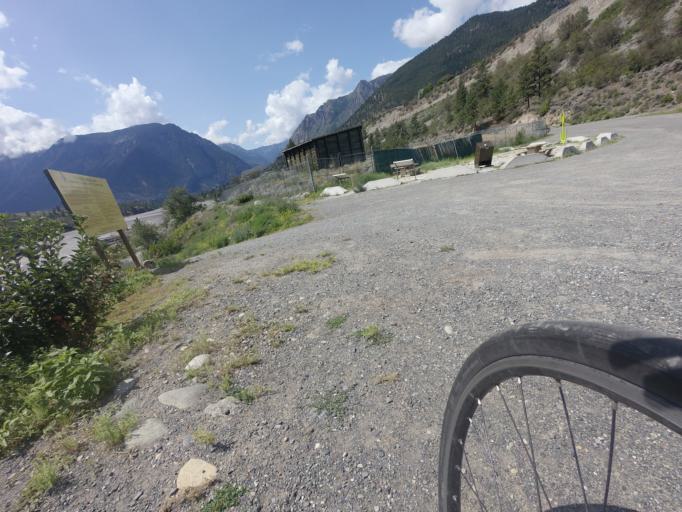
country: CA
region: British Columbia
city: Lillooet
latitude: 50.7117
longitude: -121.9128
